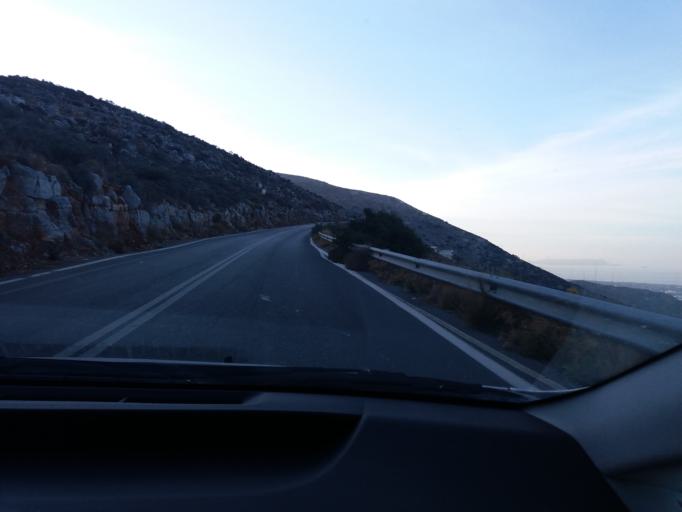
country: GR
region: Crete
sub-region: Nomos Irakleiou
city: Mokhos
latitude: 35.2755
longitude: 25.4272
